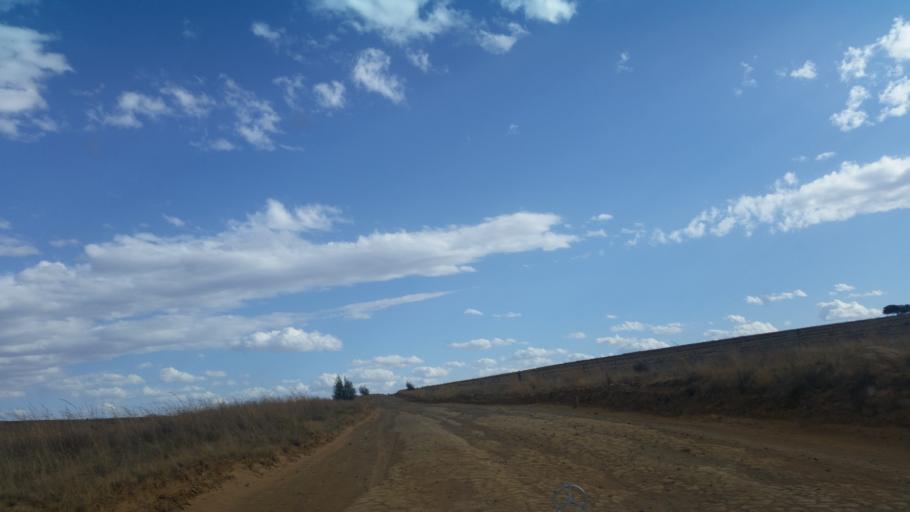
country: ZA
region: Orange Free State
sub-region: Thabo Mofutsanyana District Municipality
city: Phuthaditjhaba
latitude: -28.3524
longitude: 28.6040
